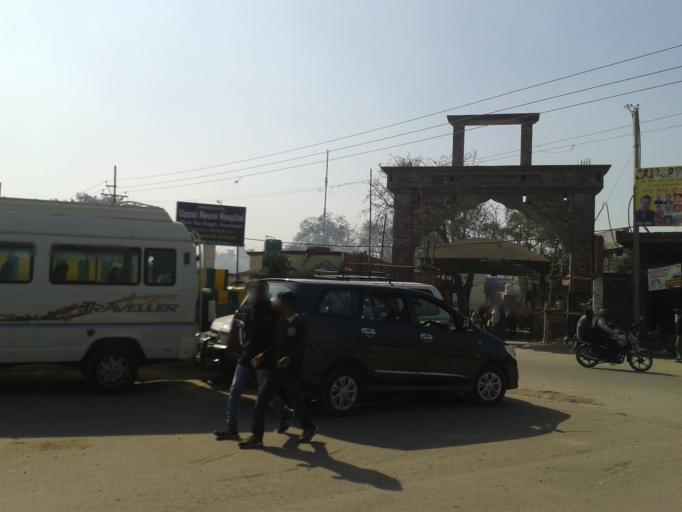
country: IN
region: Punjab
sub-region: Amritsar
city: Amritsar
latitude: 31.6279
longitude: 74.8701
